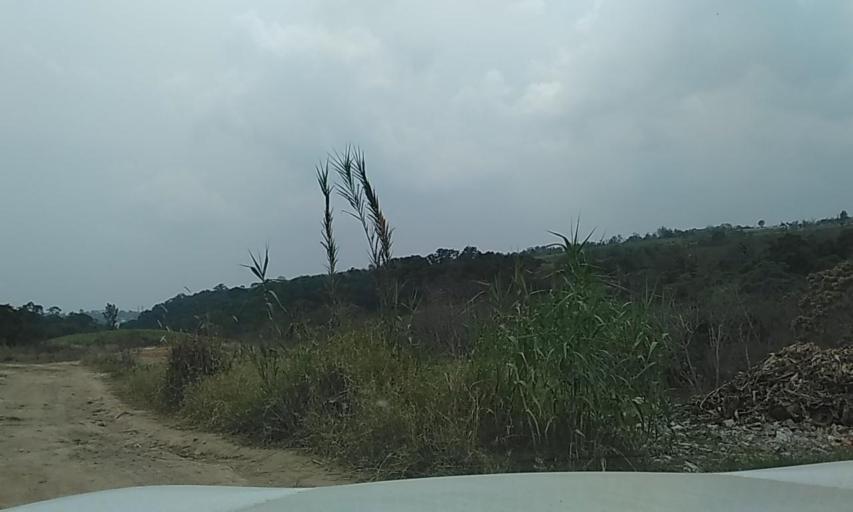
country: MX
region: Veracruz
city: El Castillo
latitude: 19.5389
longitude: -96.8763
